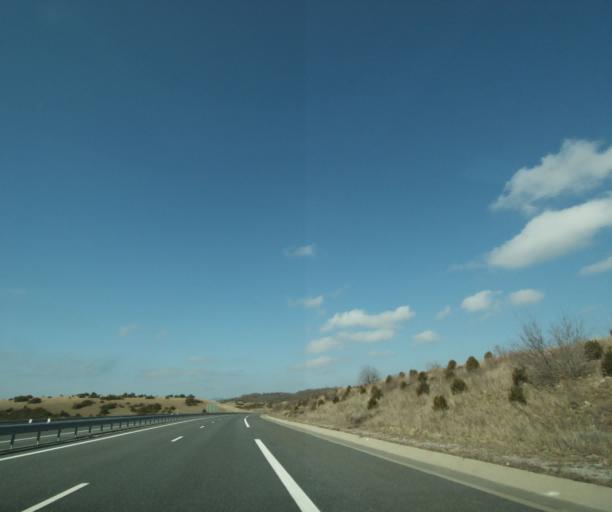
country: FR
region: Midi-Pyrenees
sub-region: Departement de l'Aveyron
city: Creissels
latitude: 44.0577
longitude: 3.0347
